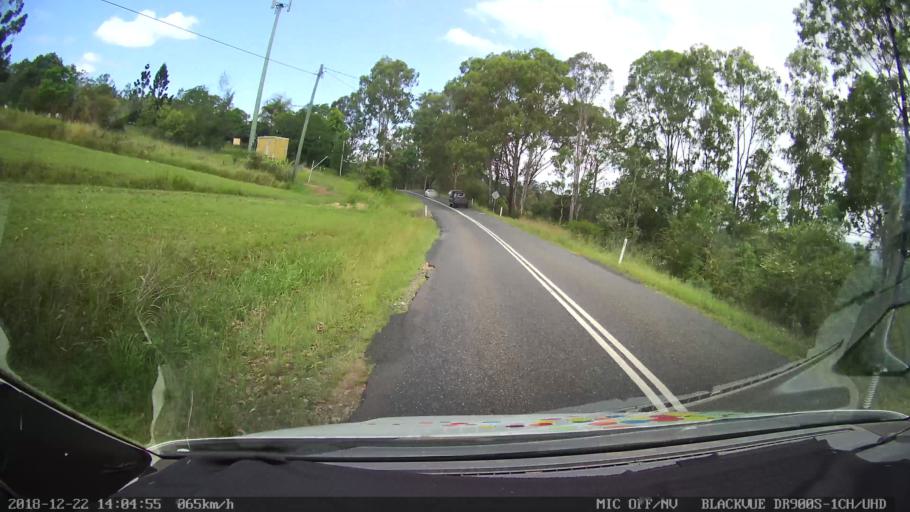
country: AU
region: New South Wales
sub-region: Clarence Valley
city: Coutts Crossing
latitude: -29.9393
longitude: 152.7261
